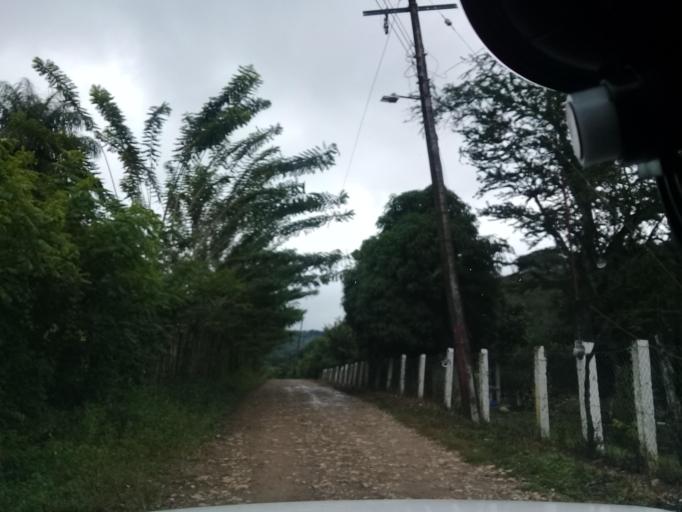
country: MX
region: Veracruz
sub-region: Chalma
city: San Pedro Coyutla
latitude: 21.2383
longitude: -98.4249
